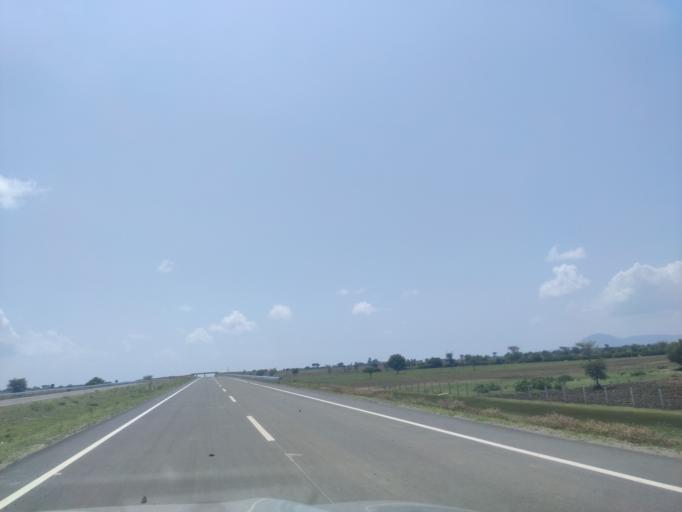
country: ET
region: Oromiya
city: Ziway
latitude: 8.2366
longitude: 38.8779
